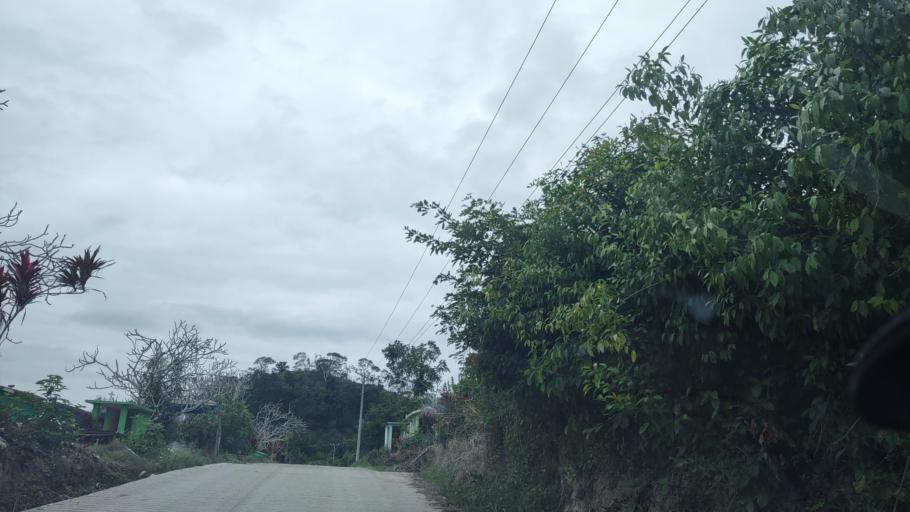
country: MX
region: Veracruz
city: Papantla de Olarte
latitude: 20.4365
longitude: -97.2713
